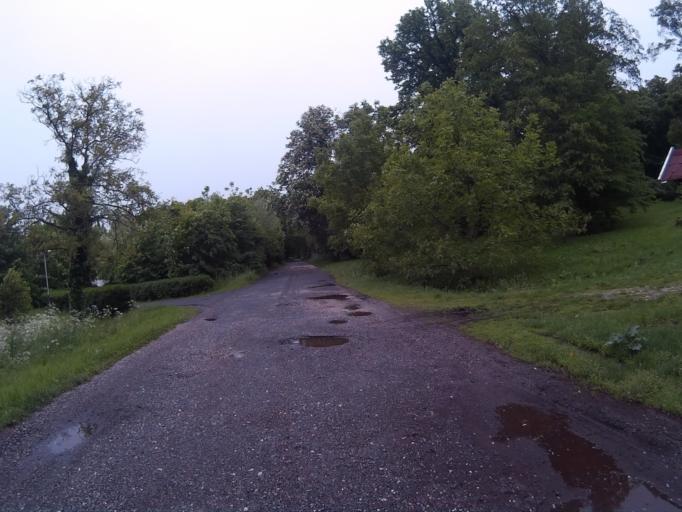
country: HU
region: Veszprem
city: Sumeg
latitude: 46.9342
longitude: 17.2934
